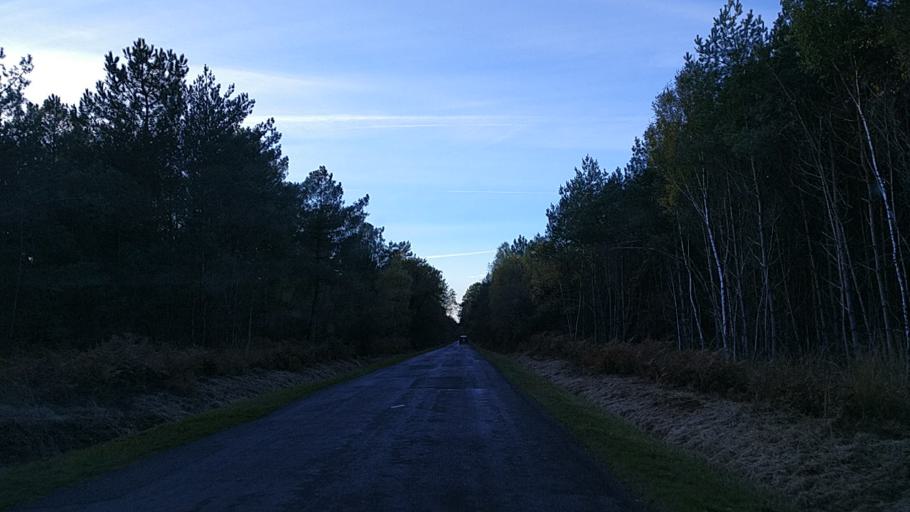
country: FR
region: Brittany
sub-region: Departement d'Ille-et-Vilaine
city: Saint-Sulpice-la-Foret
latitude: 48.1901
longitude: -1.5523
